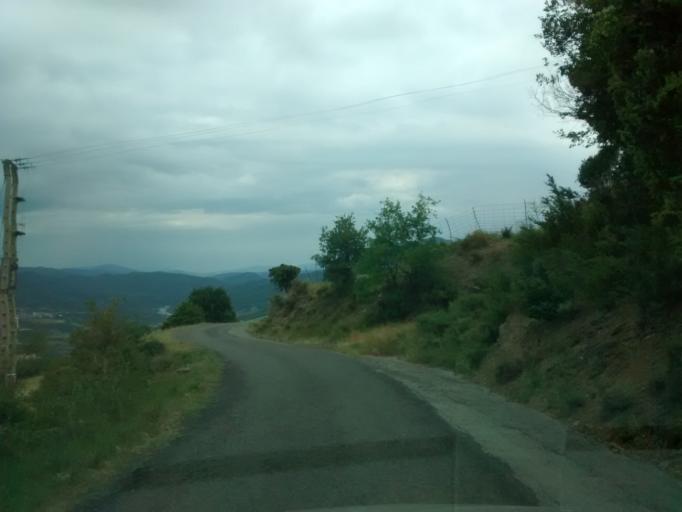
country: ES
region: Aragon
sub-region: Provincia de Huesca
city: Puertolas
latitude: 42.5387
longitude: 0.1337
